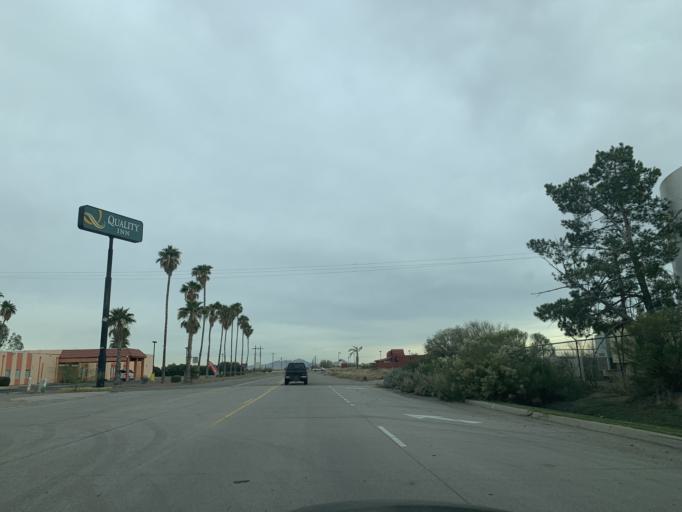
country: US
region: Arizona
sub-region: Pinal County
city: Arizona City
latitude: 32.8136
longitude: -111.6710
